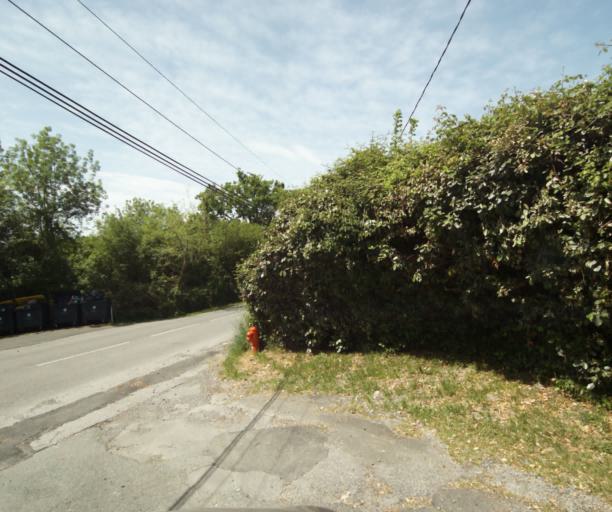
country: FR
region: Aquitaine
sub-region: Departement des Pyrenees-Atlantiques
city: Mouguerre
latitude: 43.4558
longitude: -1.4299
